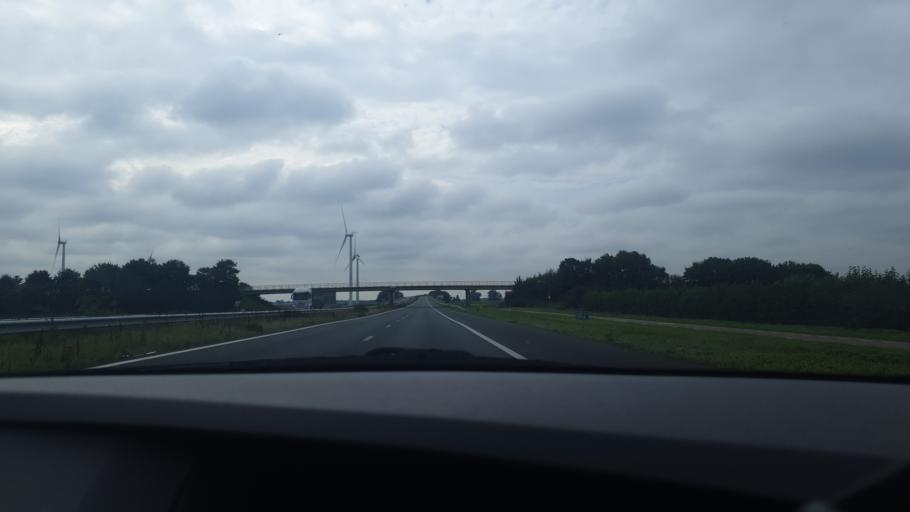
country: NL
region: North Brabant
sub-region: Gemeente Steenbergen
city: Dinteloord
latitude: 51.6508
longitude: 4.4071
